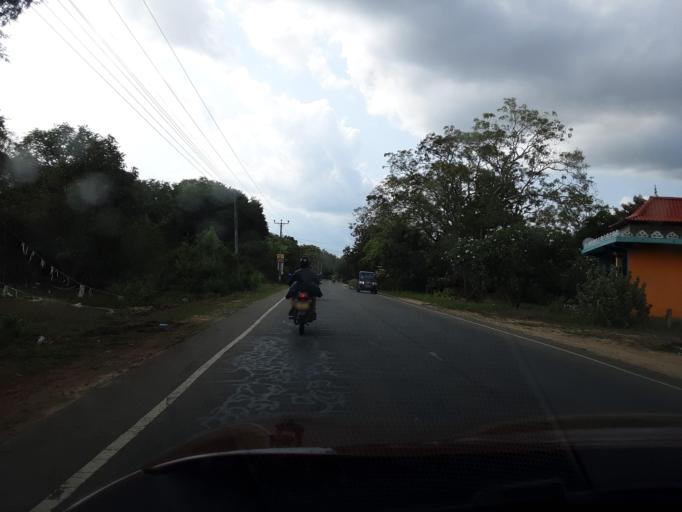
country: LK
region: Uva
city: Haputale
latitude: 6.5200
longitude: 81.1261
